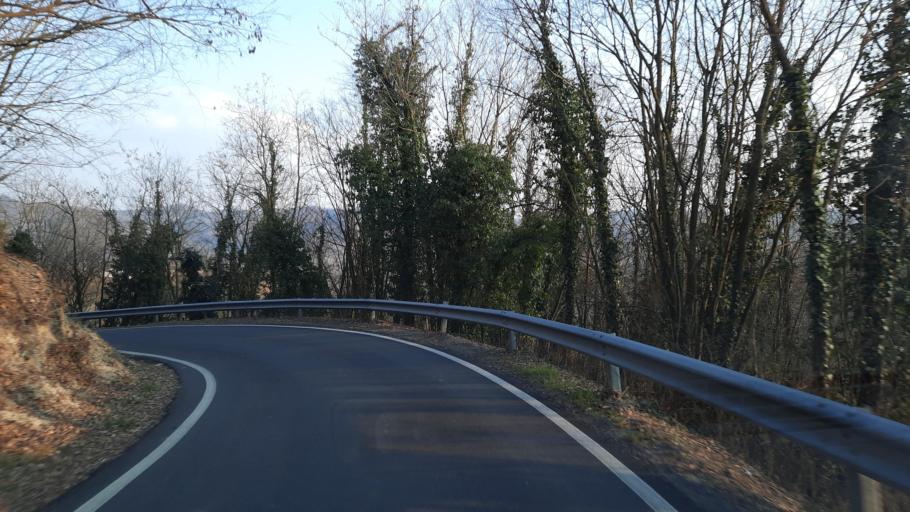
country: IT
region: Piedmont
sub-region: Provincia di Alessandria
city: Odalengo Grande
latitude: 45.1027
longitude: 8.1744
